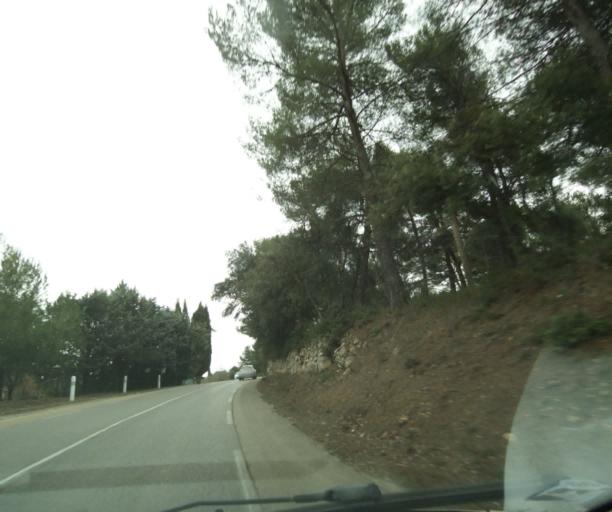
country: FR
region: Provence-Alpes-Cote d'Azur
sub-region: Departement des Bouches-du-Rhone
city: Peyrolles-en-Provence
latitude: 43.6445
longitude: 5.6053
